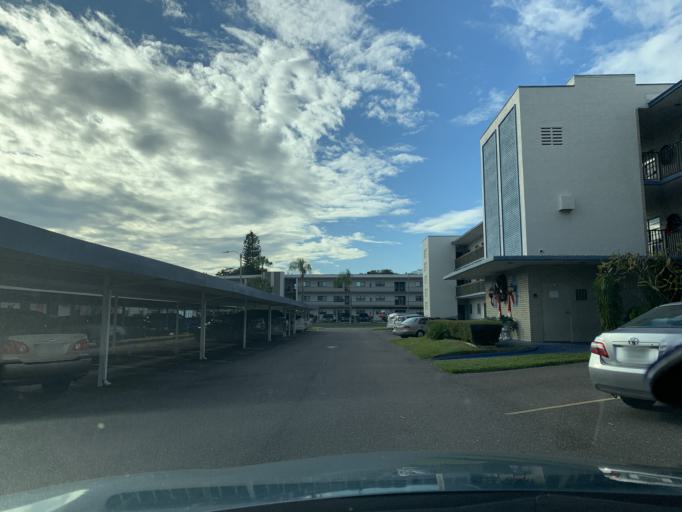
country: US
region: Florida
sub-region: Pinellas County
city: Kenneth City
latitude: 27.8256
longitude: -82.7458
